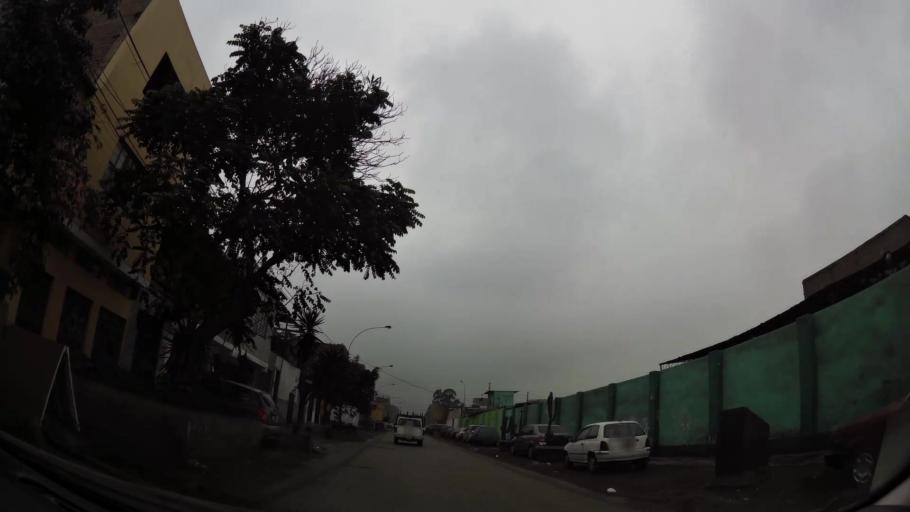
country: PE
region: Lima
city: Lima
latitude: -12.0651
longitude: -77.0260
